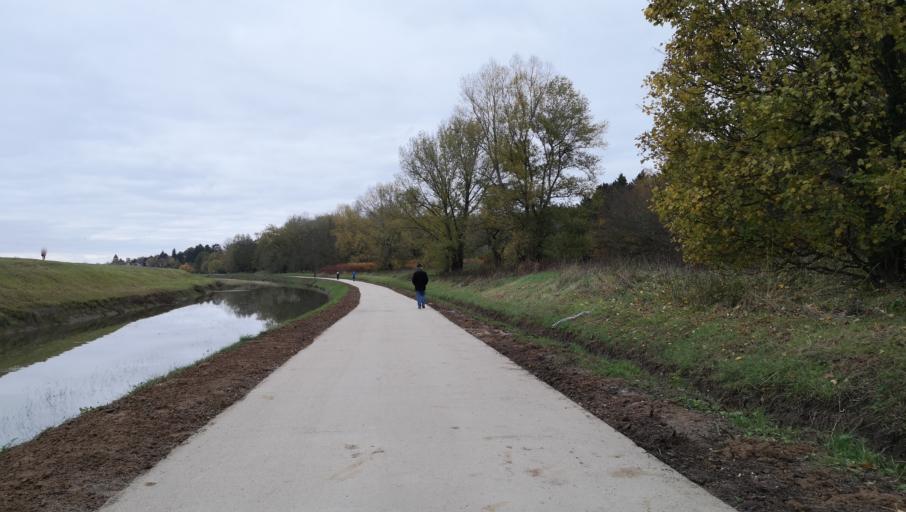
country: FR
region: Centre
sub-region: Departement du Loiret
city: Saint-Jean-de-Braye
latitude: 47.9016
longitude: 1.9819
